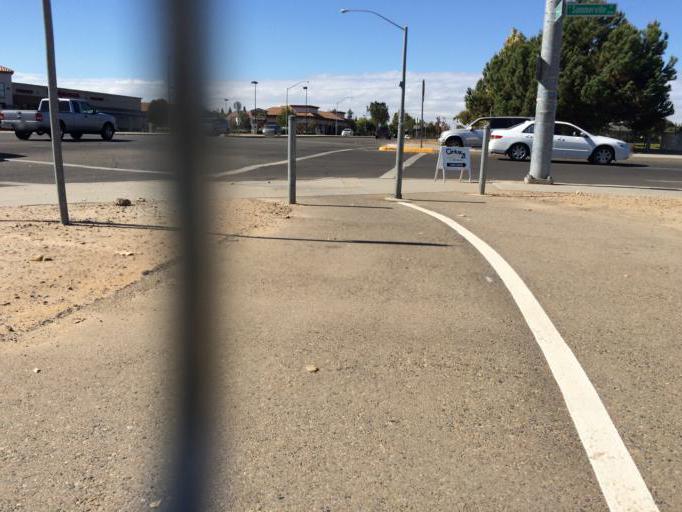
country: US
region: California
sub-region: Fresno County
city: Clovis
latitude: 36.8669
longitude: -119.7385
